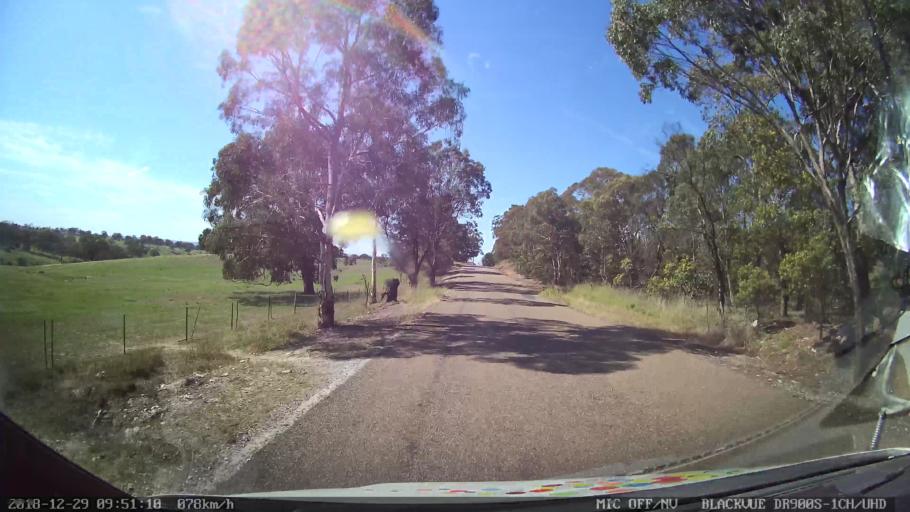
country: AU
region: New South Wales
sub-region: Goulburn Mulwaree
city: Goulburn
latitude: -34.7293
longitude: 149.4616
